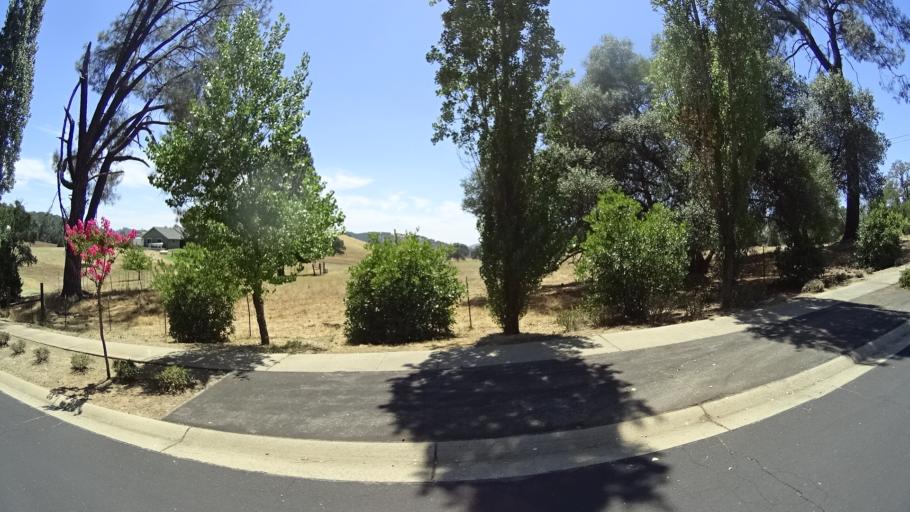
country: US
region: California
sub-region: Calaveras County
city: Angels Camp
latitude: 38.0620
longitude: -120.5528
